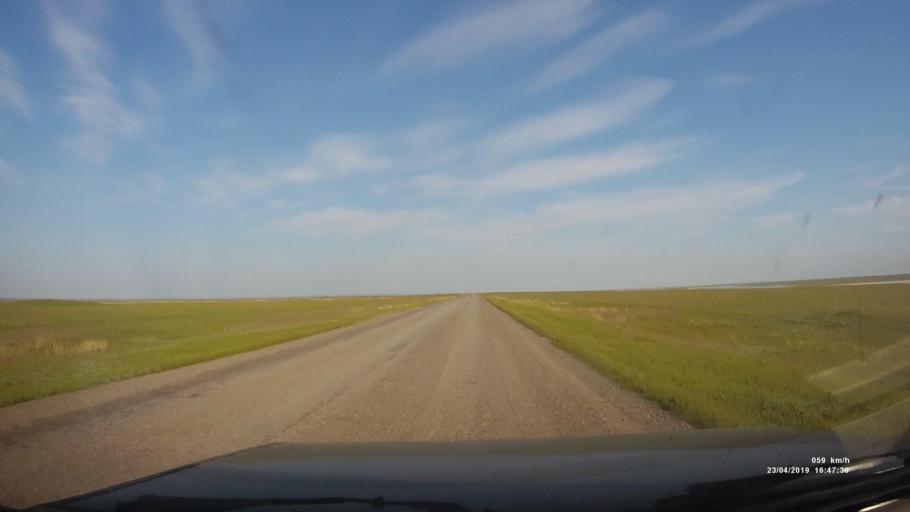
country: RU
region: Kalmykiya
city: Priyutnoye
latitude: 46.3385
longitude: 43.2490
